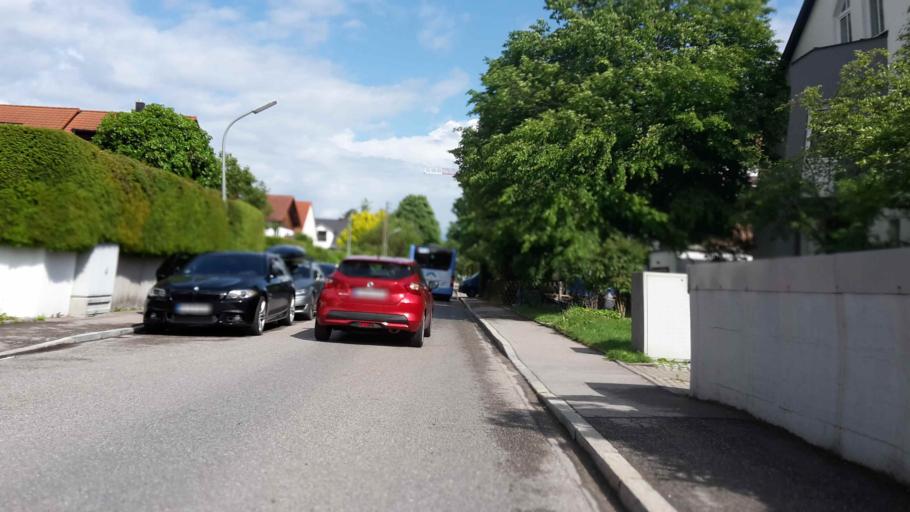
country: DE
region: Bavaria
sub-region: Upper Bavaria
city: Karlsfeld
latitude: 48.2014
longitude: 11.5080
